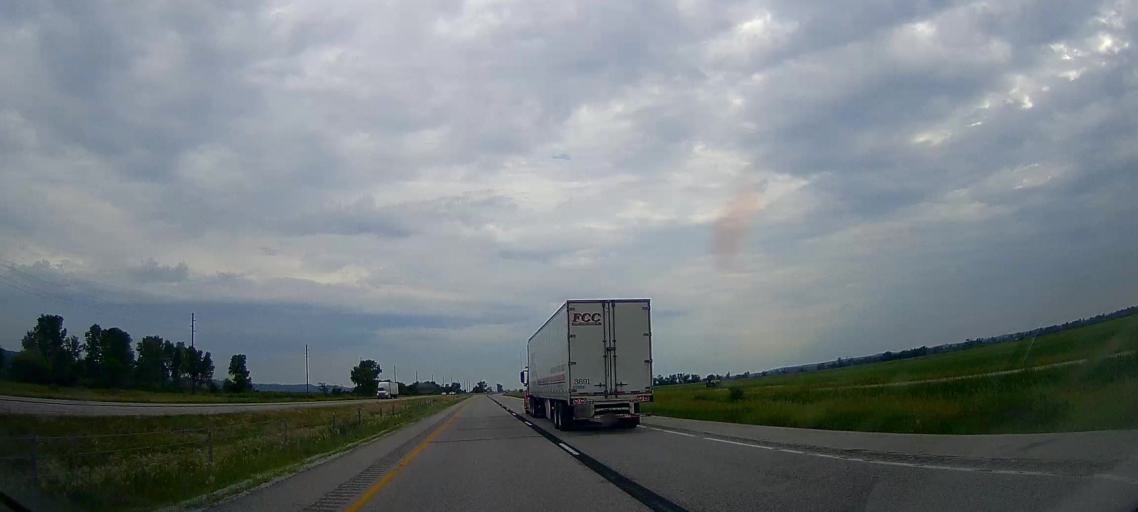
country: US
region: Iowa
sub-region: Harrison County
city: Missouri Valley
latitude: 41.4766
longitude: -95.8999
